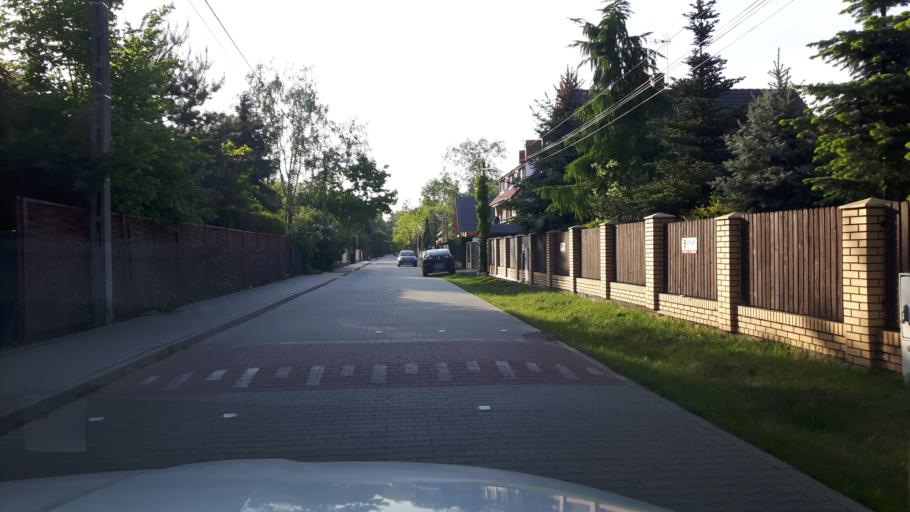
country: PL
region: Masovian Voivodeship
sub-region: Warszawa
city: Rembertow
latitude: 52.2746
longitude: 21.1580
